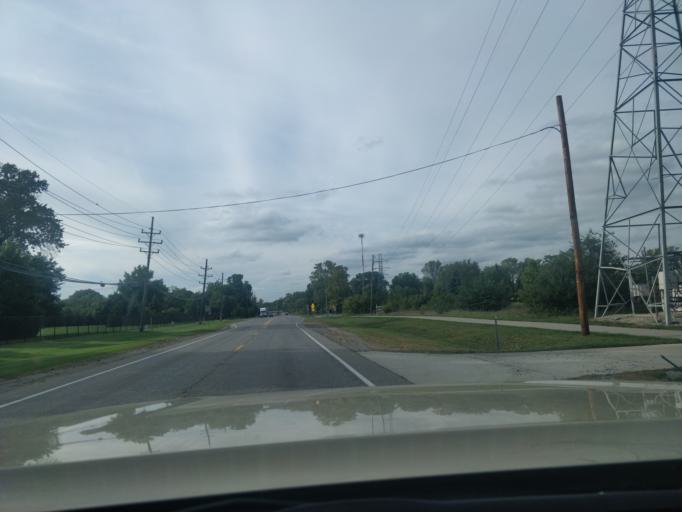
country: US
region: Michigan
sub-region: Wayne County
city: Romulus
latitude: 42.2149
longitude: -83.4123
